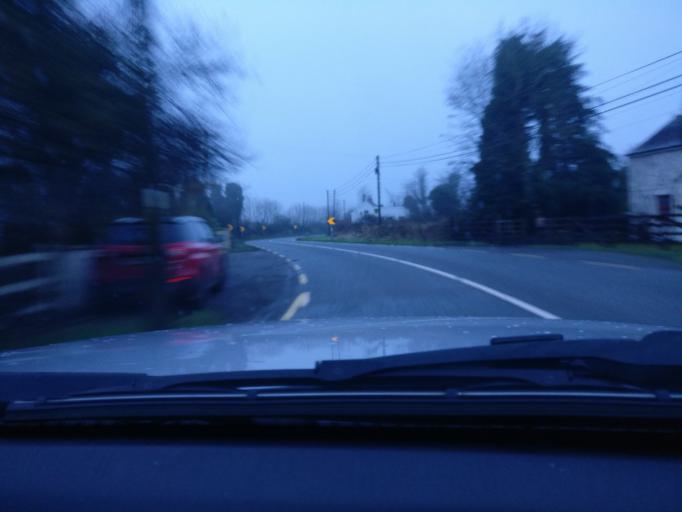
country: IE
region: Leinster
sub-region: An Mhi
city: Athboy
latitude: 53.6124
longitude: -6.9449
